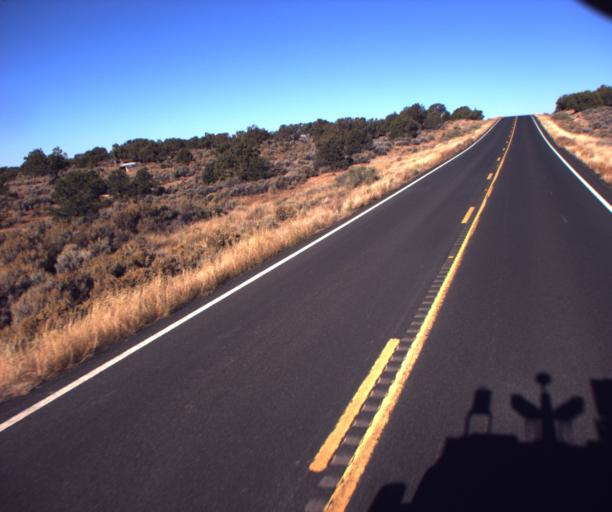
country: US
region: Arizona
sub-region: Apache County
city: Ganado
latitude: 35.7634
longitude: -109.7859
